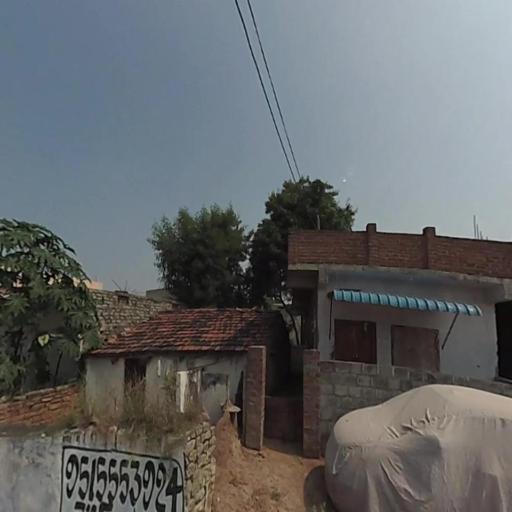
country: IN
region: Telangana
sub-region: Nalgonda
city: Nalgonda
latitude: 17.1871
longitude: 79.1271
